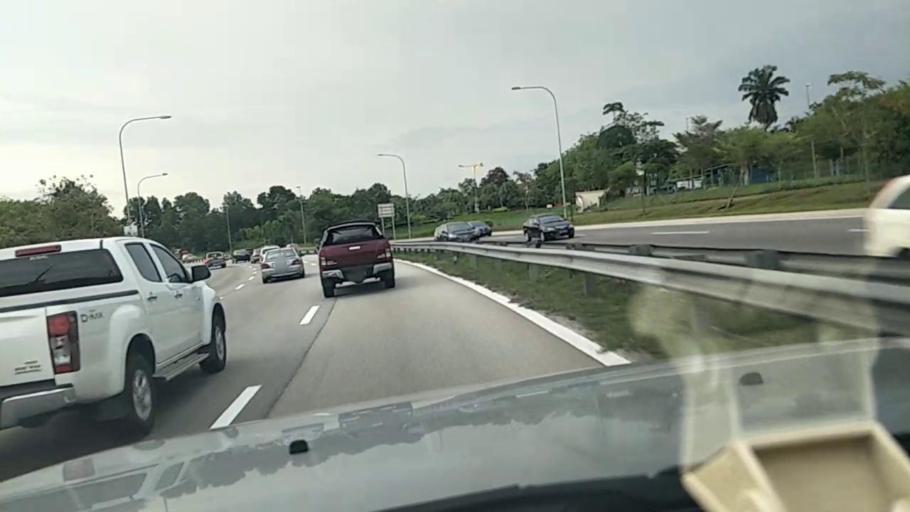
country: MY
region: Selangor
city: Shah Alam
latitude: 3.0980
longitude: 101.4825
